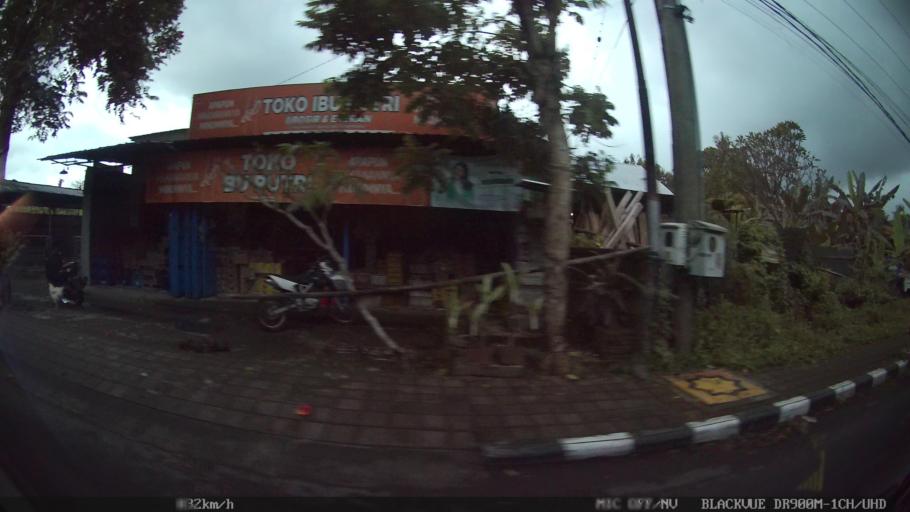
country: ID
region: Bali
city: Banjar Sempidi
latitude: -8.5164
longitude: 115.2054
